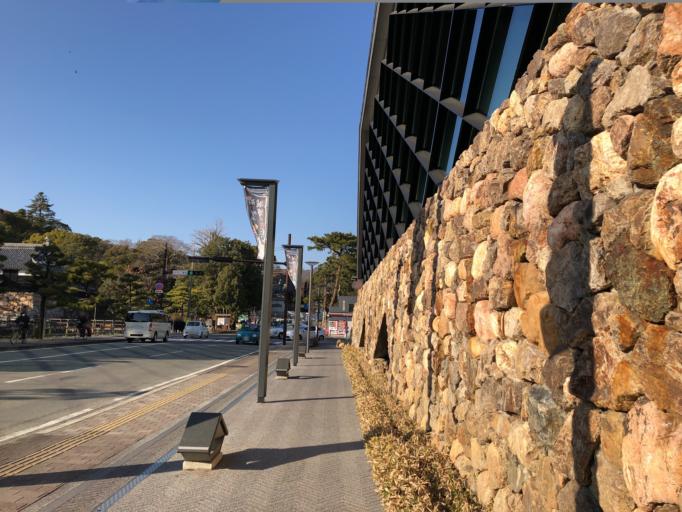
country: JP
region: Kochi
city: Kochi-shi
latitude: 33.5601
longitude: 133.5339
